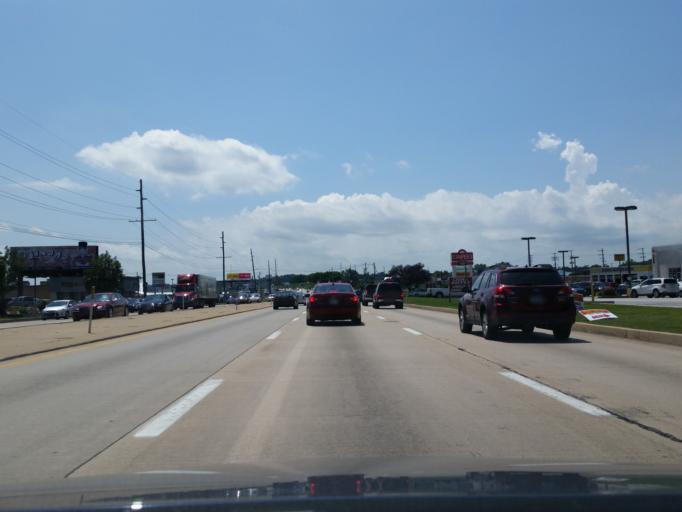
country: US
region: Pennsylvania
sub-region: York County
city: North York
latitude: 39.9798
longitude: -76.7537
